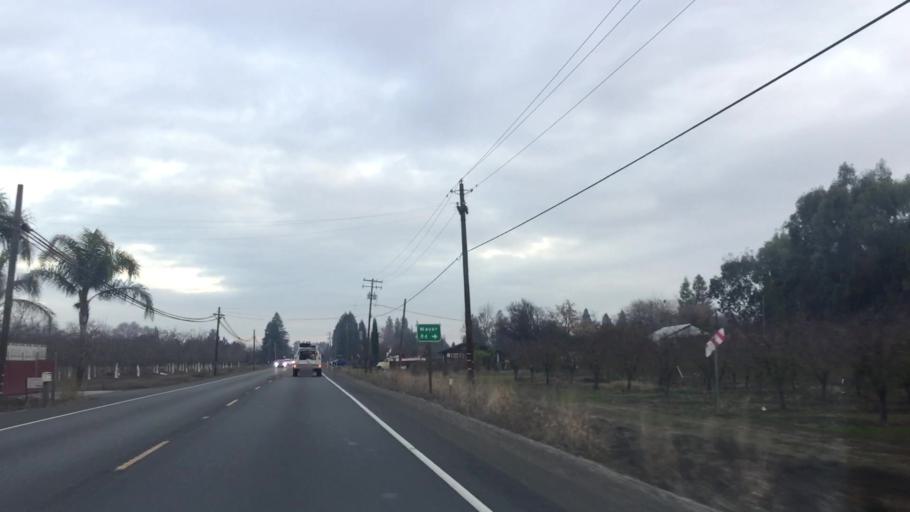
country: US
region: California
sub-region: Yuba County
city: Marysville
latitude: 39.1853
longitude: -121.5933
